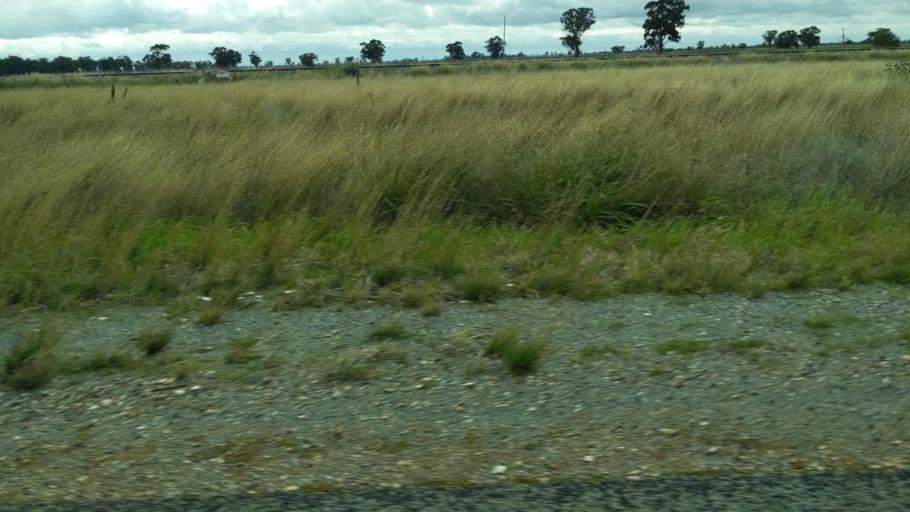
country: AU
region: New South Wales
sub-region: Coolamon
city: Coolamon
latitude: -34.7600
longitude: 146.8820
